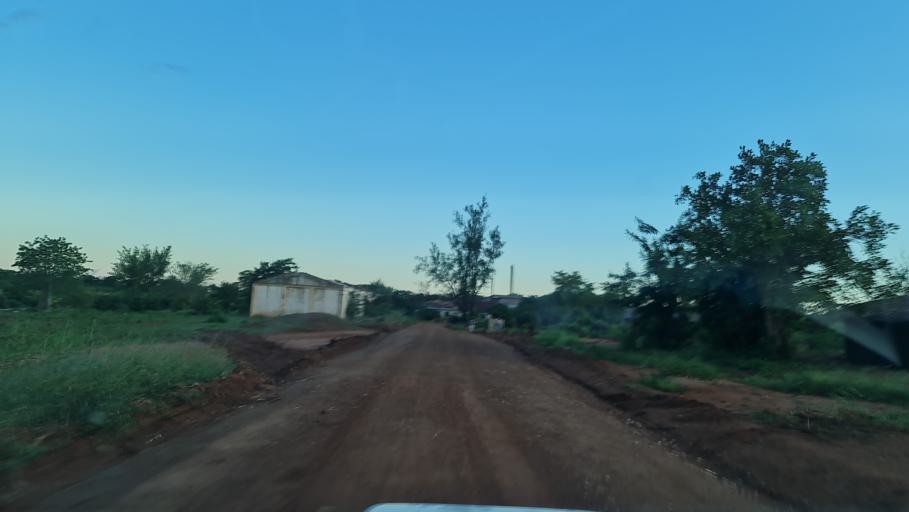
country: MZ
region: Nampula
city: Ilha de Mocambique
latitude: -14.9834
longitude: 40.0945
